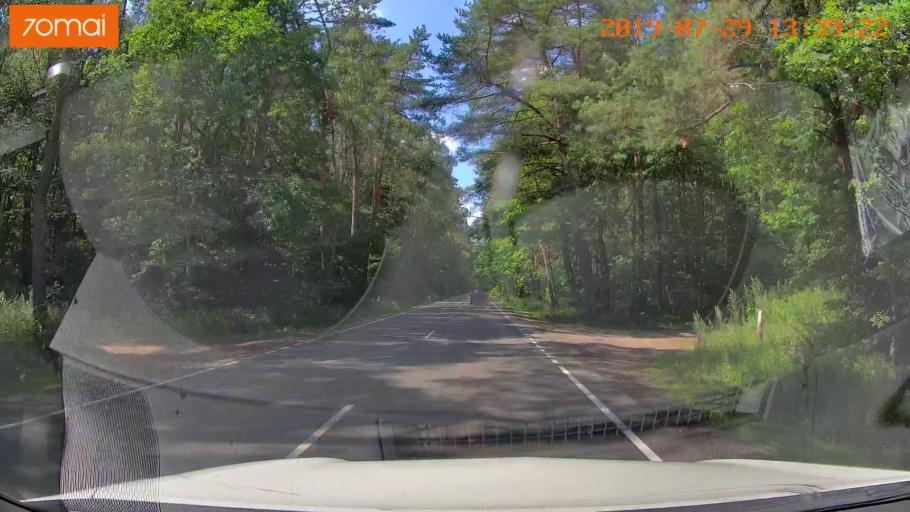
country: RU
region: Kaliningrad
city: Svetlyy
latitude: 54.7238
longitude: 20.1545
